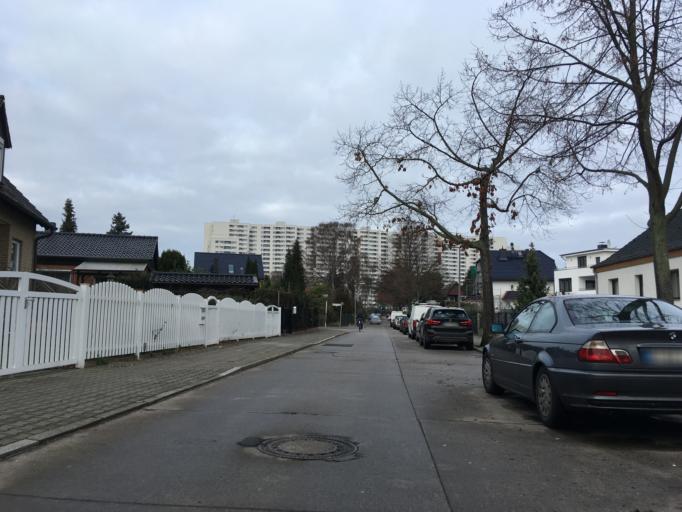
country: DE
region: Berlin
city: Markisches Viertel
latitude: 52.5929
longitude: 13.3555
